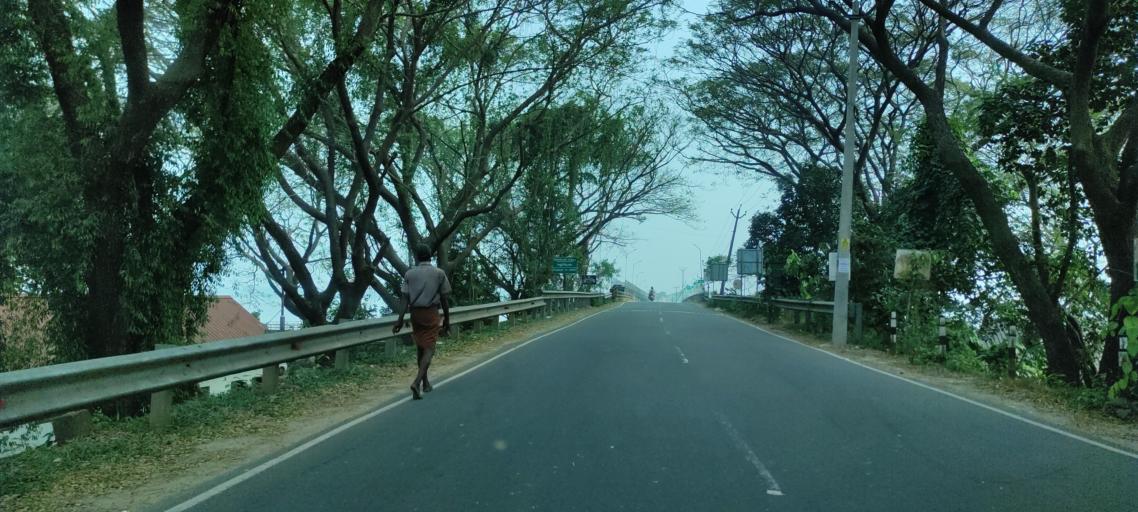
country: IN
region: Kerala
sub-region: Alappuzha
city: Shertallai
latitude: 9.6766
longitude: 76.3933
